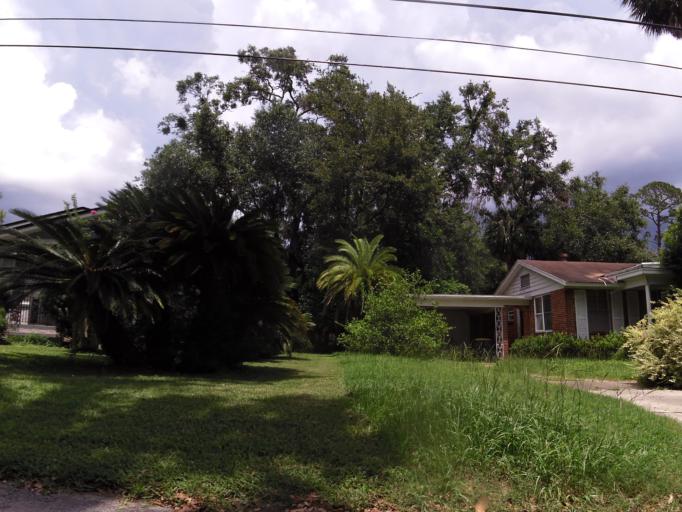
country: US
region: Florida
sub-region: Duval County
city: Jacksonville
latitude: 30.3013
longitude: -81.6973
